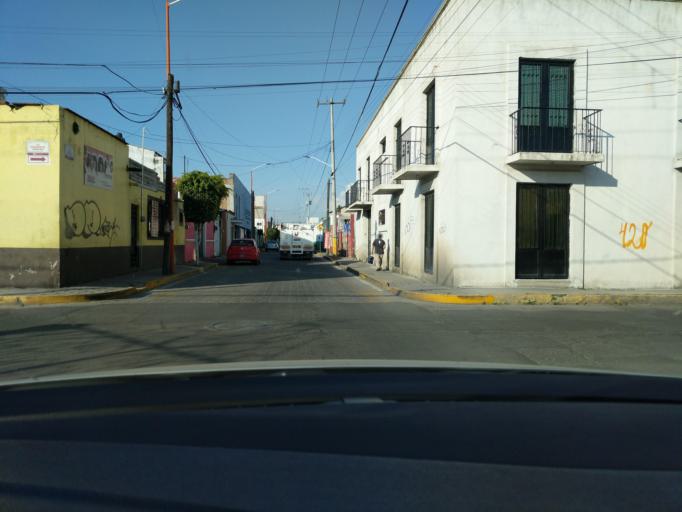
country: MX
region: Puebla
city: Cholula
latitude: 19.0573
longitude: -98.3111
